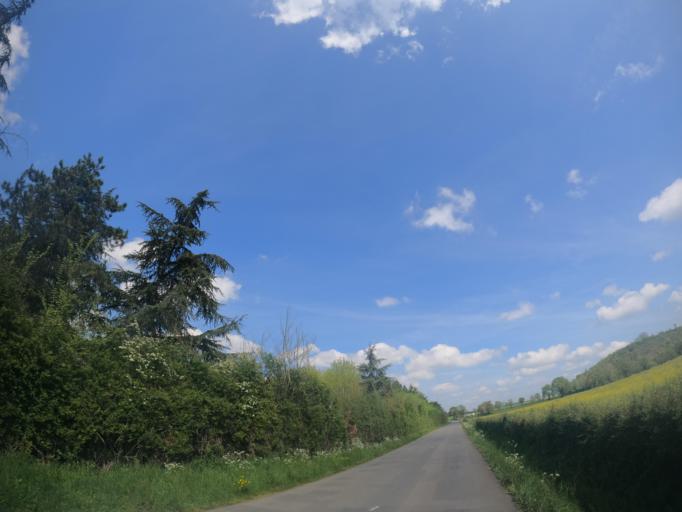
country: FR
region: Poitou-Charentes
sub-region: Departement des Deux-Sevres
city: Saint-Varent
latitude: 46.8663
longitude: -0.2452
